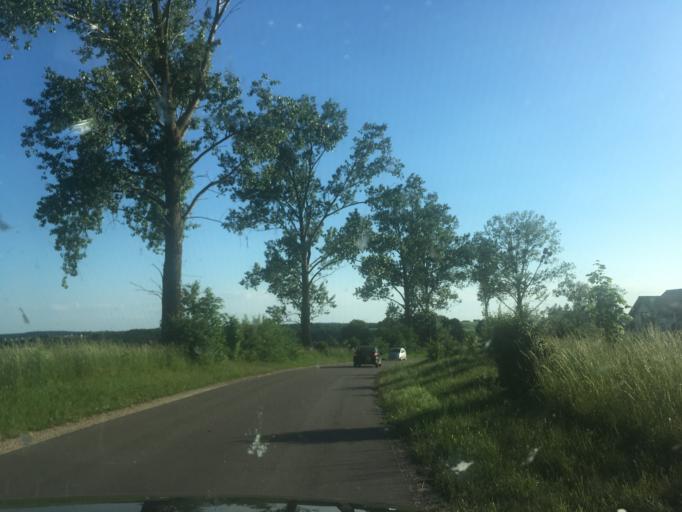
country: PL
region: Warmian-Masurian Voivodeship
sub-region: Powiat ostrodzki
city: Ostroda
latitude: 53.6739
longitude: 20.0389
